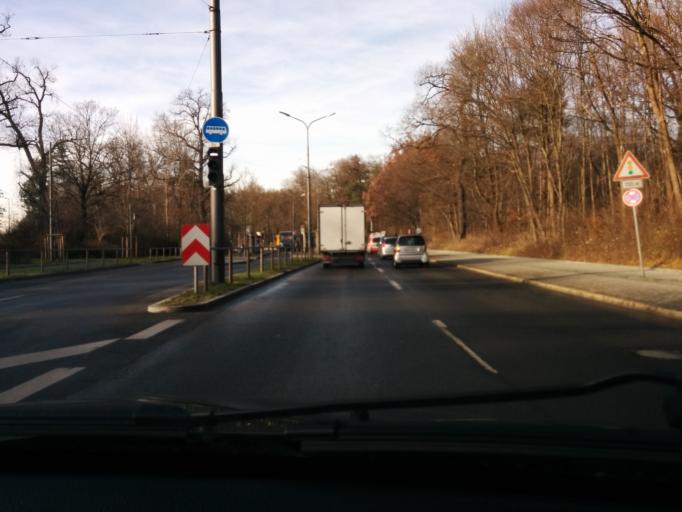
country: DE
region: Bavaria
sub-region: Upper Bavaria
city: Pasing
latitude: 48.1655
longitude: 11.4952
